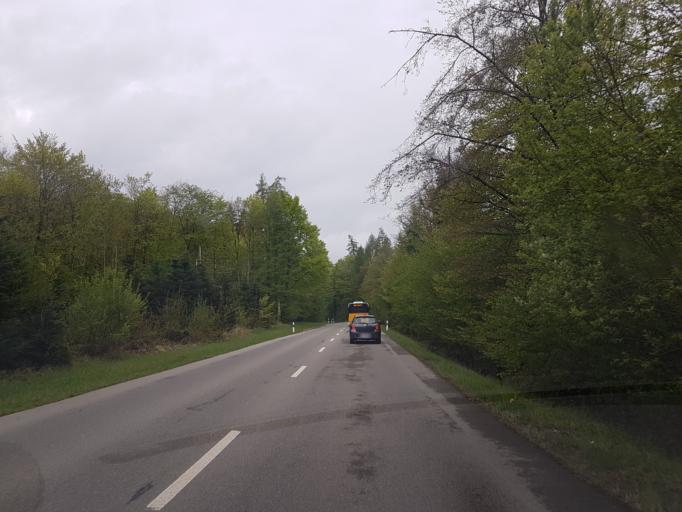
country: CH
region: Zurich
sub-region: Bezirk Dietikon
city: Schlieren / Kamp
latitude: 47.3803
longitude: 8.4467
